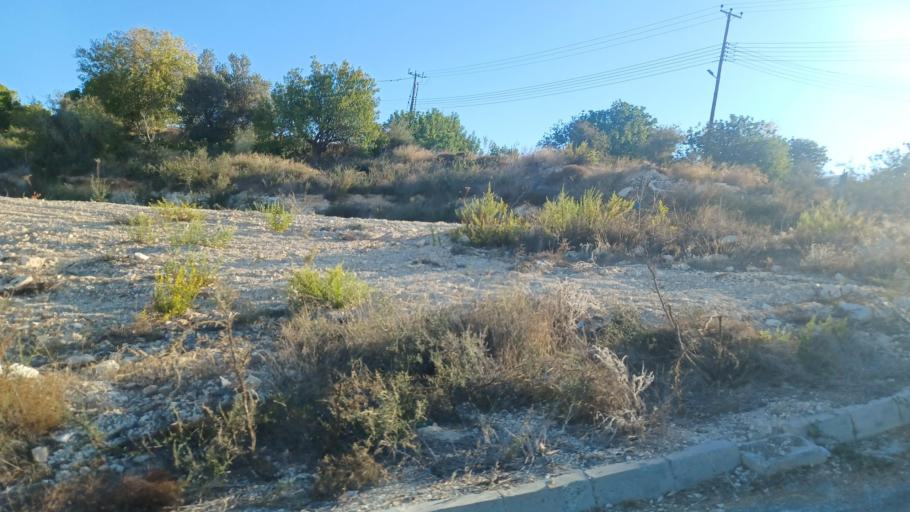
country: CY
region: Pafos
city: Mesogi
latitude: 34.7985
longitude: 32.4870
